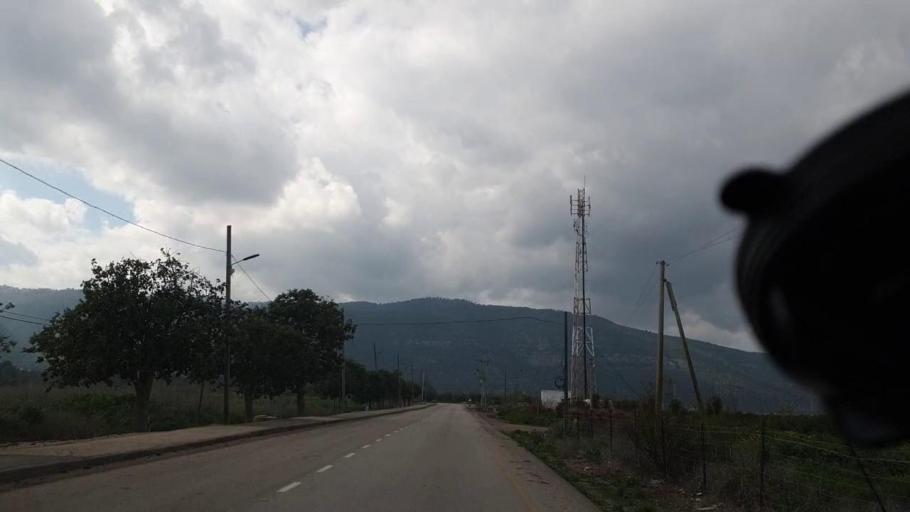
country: IL
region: Haifa
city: Rekhasim
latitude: 32.7556
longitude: 35.0883
